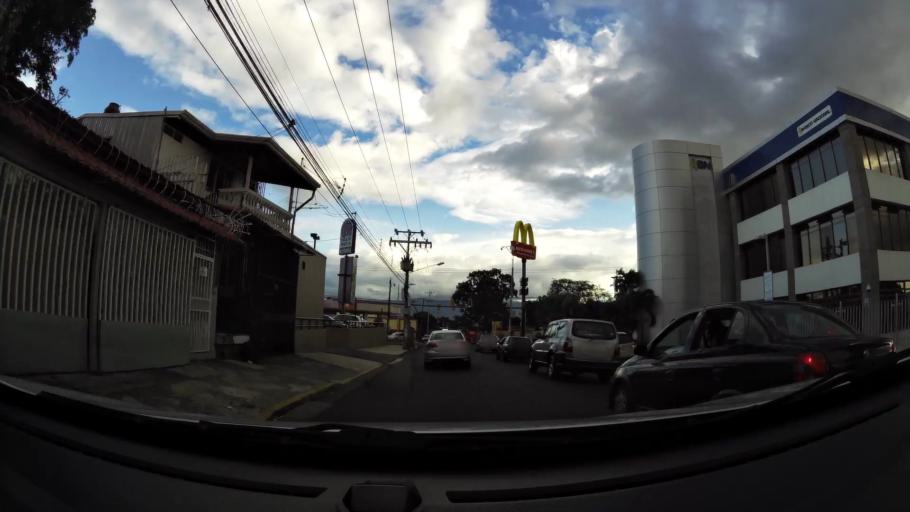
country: CR
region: Alajuela
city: Alajuela
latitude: 10.0131
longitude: -84.2103
